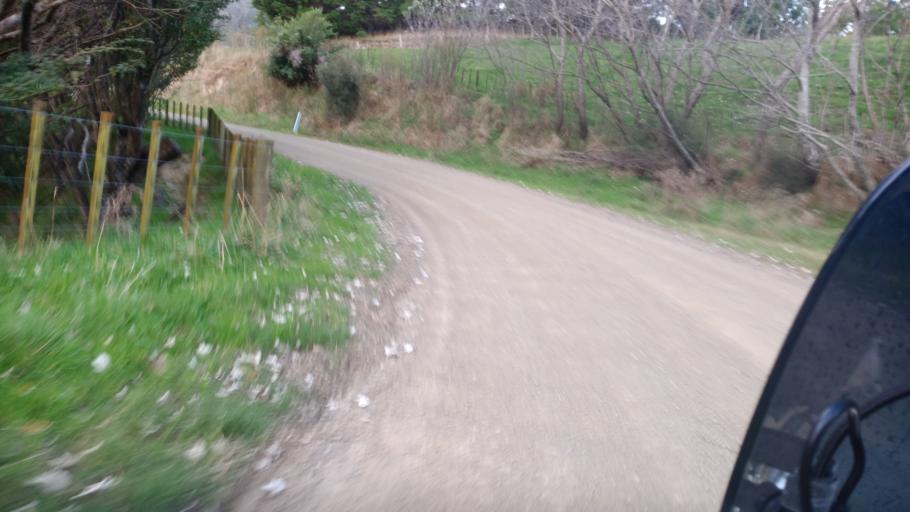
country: NZ
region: Gisborne
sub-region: Gisborne District
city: Gisborne
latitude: -38.4609
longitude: 177.6323
